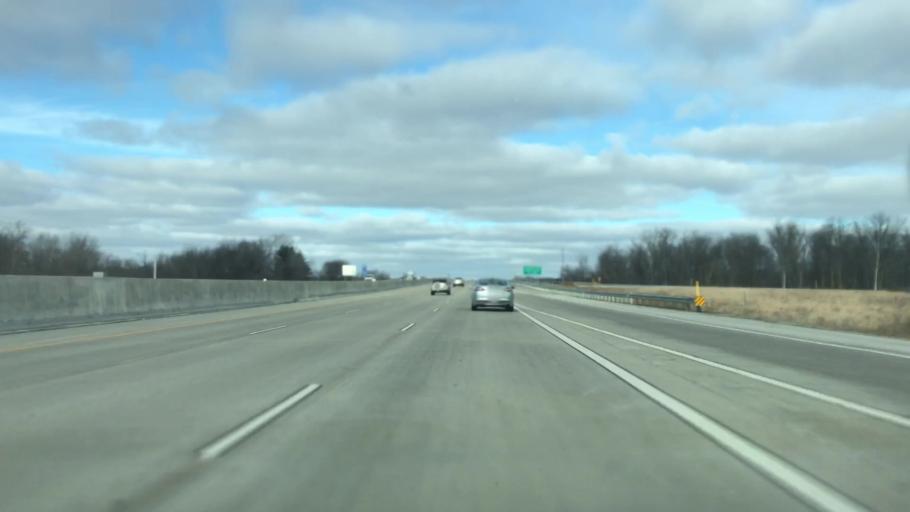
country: US
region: Wisconsin
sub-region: Brown County
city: Ashwaubenon
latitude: 44.4798
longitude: -88.0799
